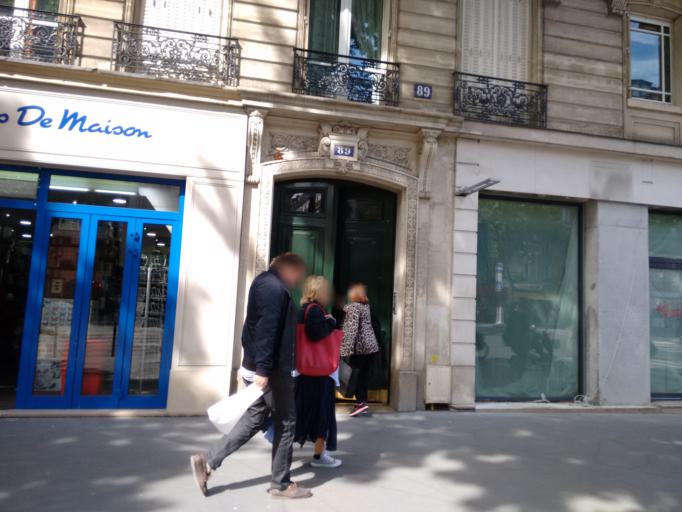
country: FR
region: Ile-de-France
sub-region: Paris
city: Paris
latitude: 48.8433
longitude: 2.3263
